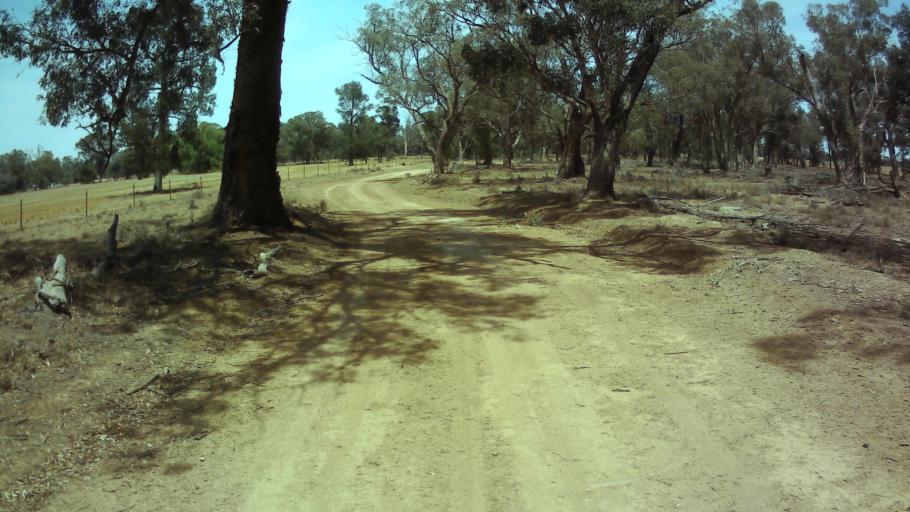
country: AU
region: New South Wales
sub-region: Weddin
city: Grenfell
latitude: -34.0329
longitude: 147.9304
